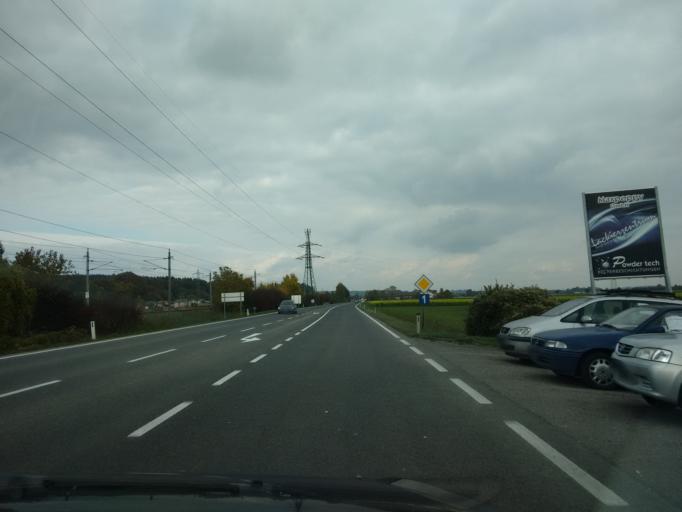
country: AT
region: Upper Austria
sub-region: Politischer Bezirk Vocklabruck
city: Redlham
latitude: 48.0278
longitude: 13.7357
